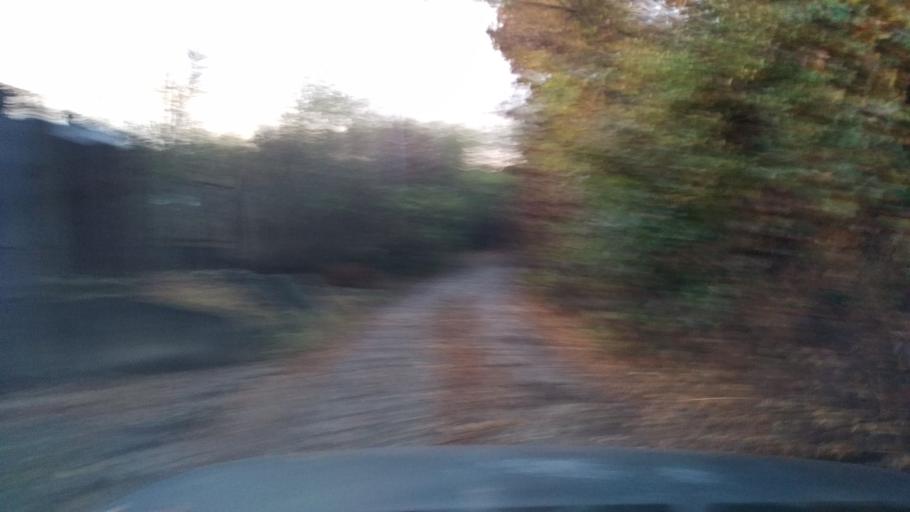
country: HU
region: Pest
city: Nagykovacsi
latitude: 47.6640
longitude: 19.0000
